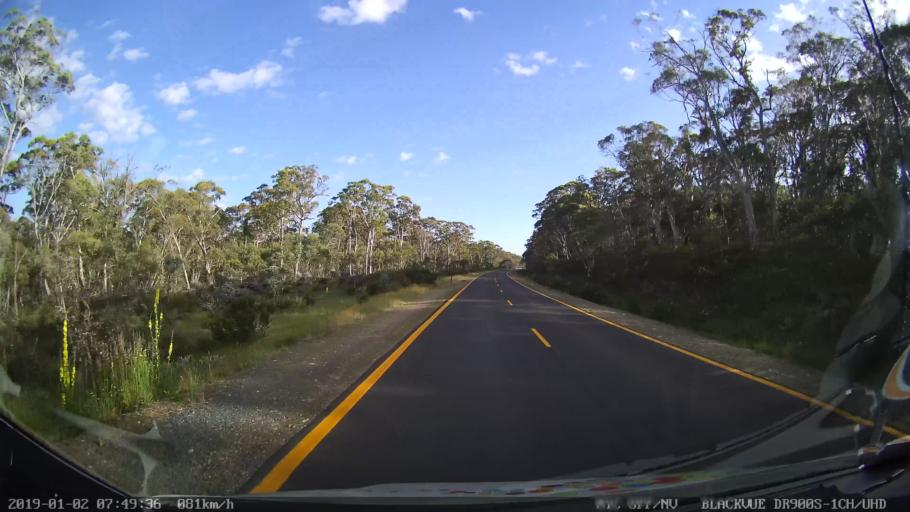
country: AU
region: New South Wales
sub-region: Tumut Shire
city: Tumut
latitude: -35.7397
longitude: 148.5228
